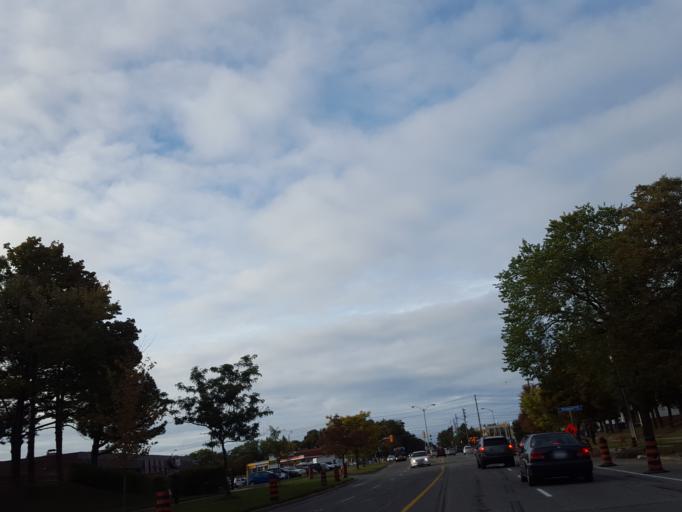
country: CA
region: Ontario
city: Scarborough
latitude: 43.7770
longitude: -79.3070
